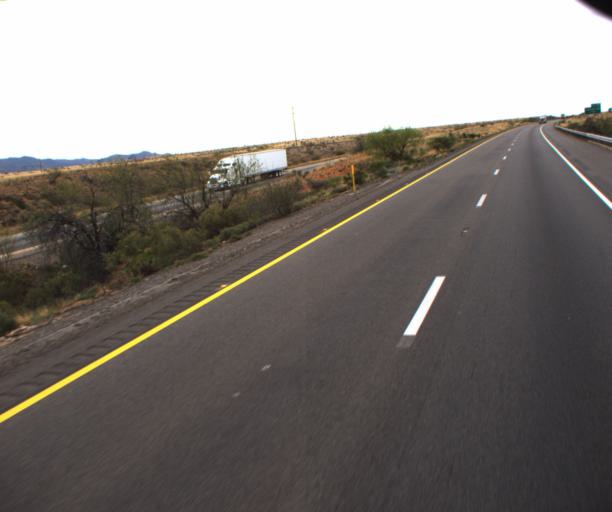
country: US
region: Arizona
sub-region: Cochise County
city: Willcox
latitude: 32.0946
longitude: -110.0355
